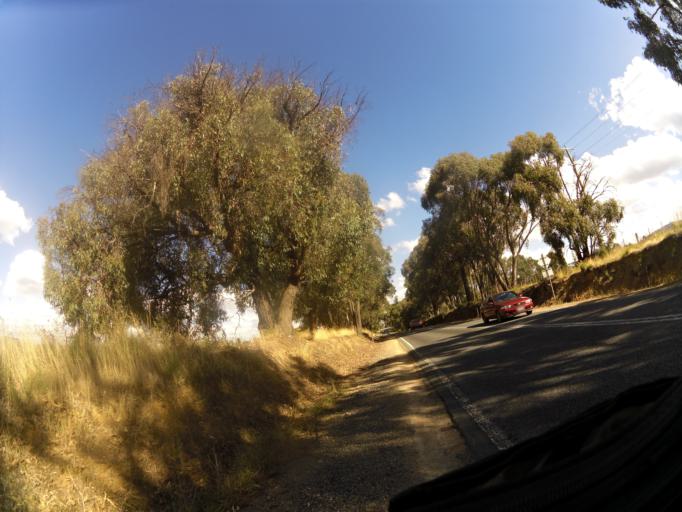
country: AU
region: Victoria
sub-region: Mansfield
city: Mansfield
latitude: -36.9217
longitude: 146.0015
